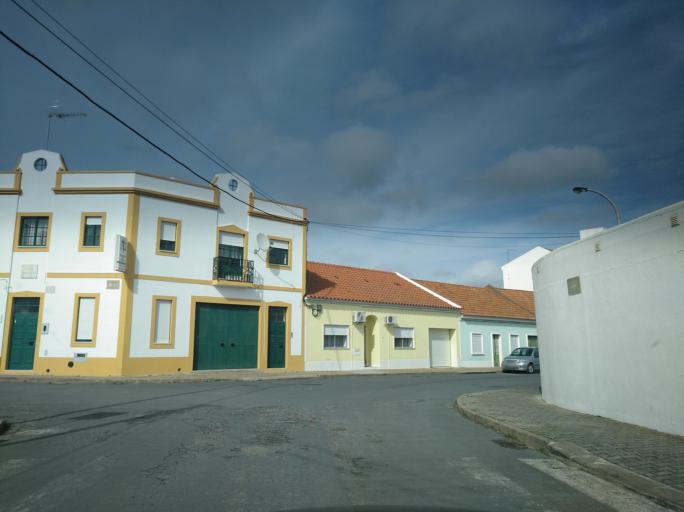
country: PT
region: Setubal
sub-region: Grandola
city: Grandola
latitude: 38.1771
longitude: -8.5609
